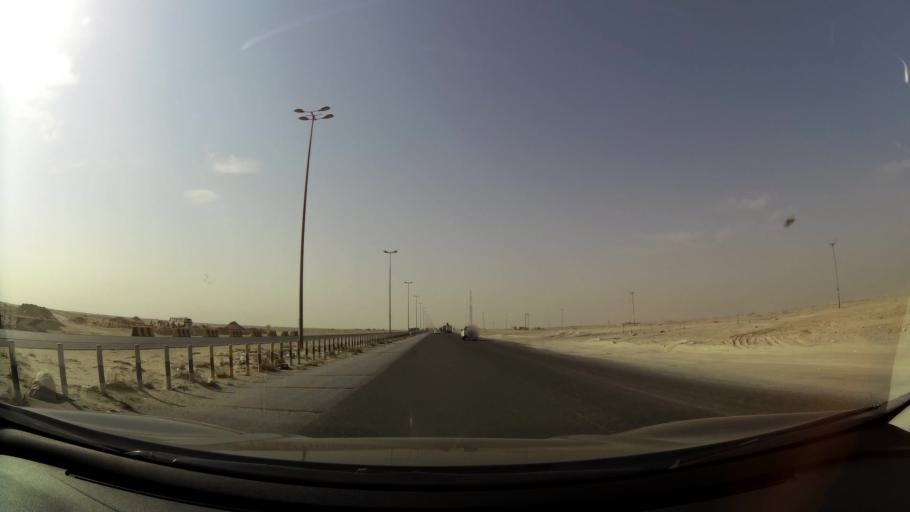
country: KW
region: Al Ahmadi
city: Al Ahmadi
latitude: 28.9116
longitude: 48.0967
